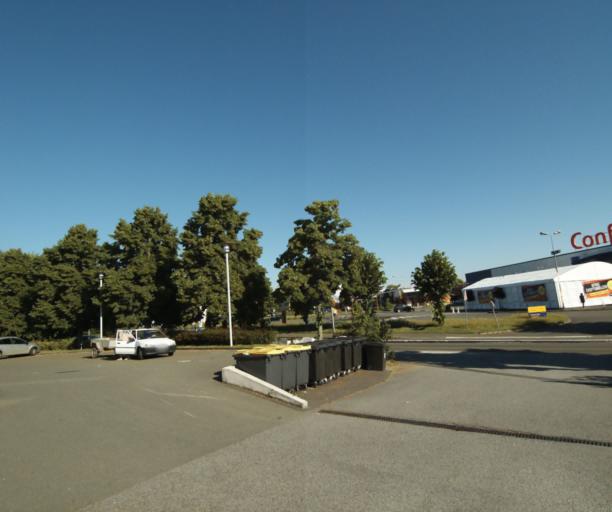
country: FR
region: Pays de la Loire
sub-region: Departement de la Mayenne
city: Laval
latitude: 48.0530
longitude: -0.7392
